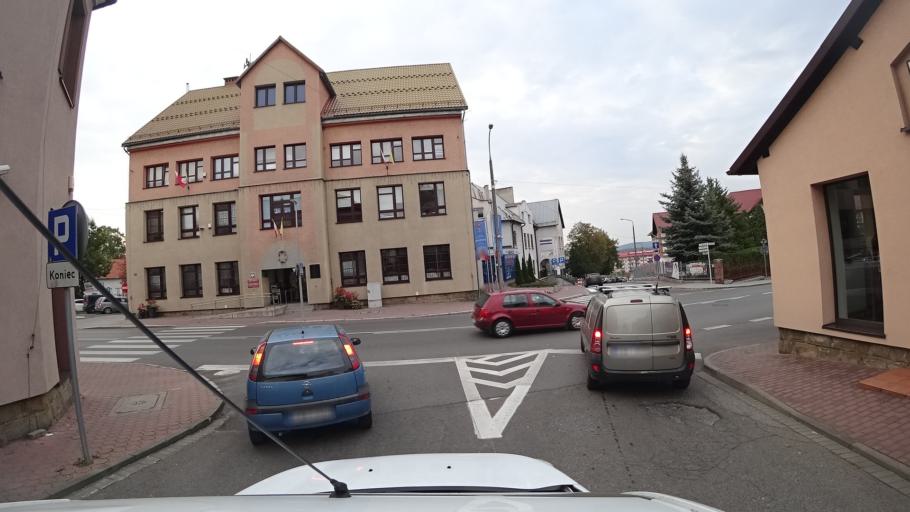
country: PL
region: Lesser Poland Voivodeship
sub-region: Powiat wadowicki
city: Kalwaria Zebrzydowska
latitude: 49.8682
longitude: 19.6780
